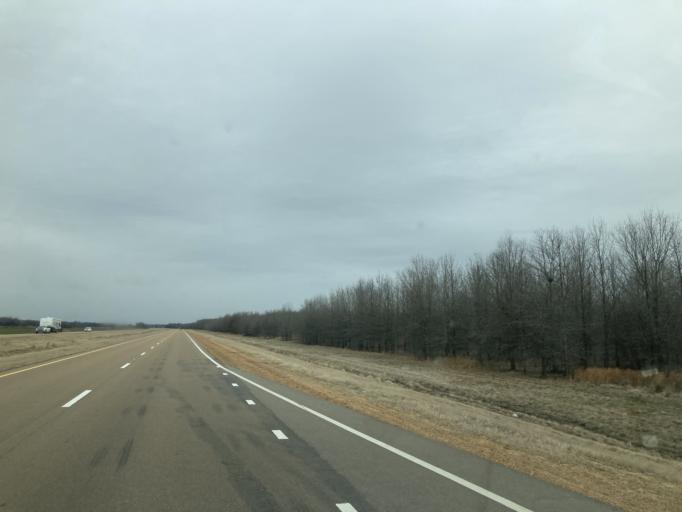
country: US
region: Mississippi
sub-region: Humphreys County
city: Belzoni
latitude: 33.0150
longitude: -90.4688
